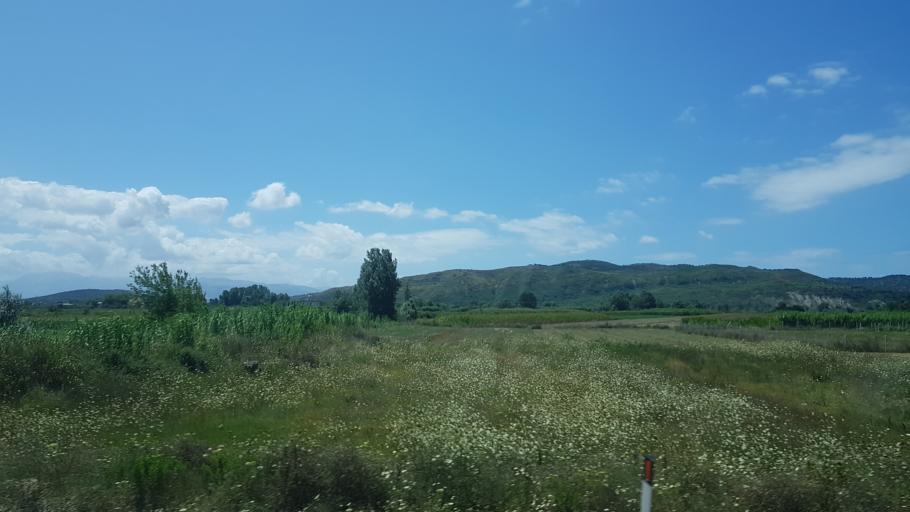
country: AL
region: Fier
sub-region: Rrethi i Fierit
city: Frakulla e Madhe
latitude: 40.6074
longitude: 19.5390
